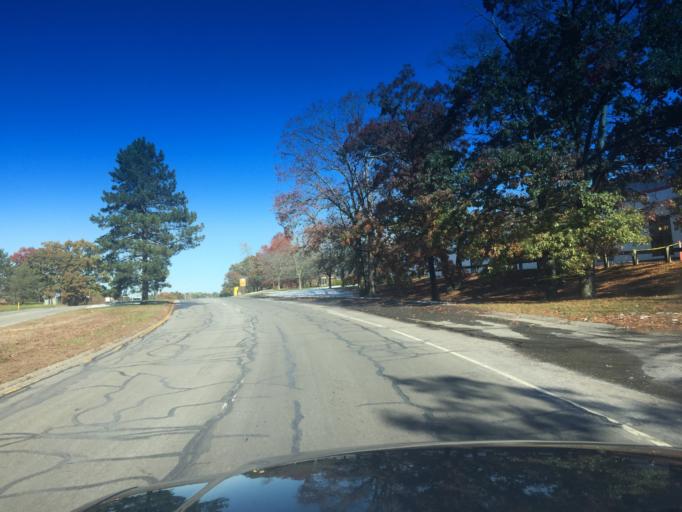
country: US
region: Massachusetts
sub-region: Bristol County
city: Norton
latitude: 41.9542
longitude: -71.1366
